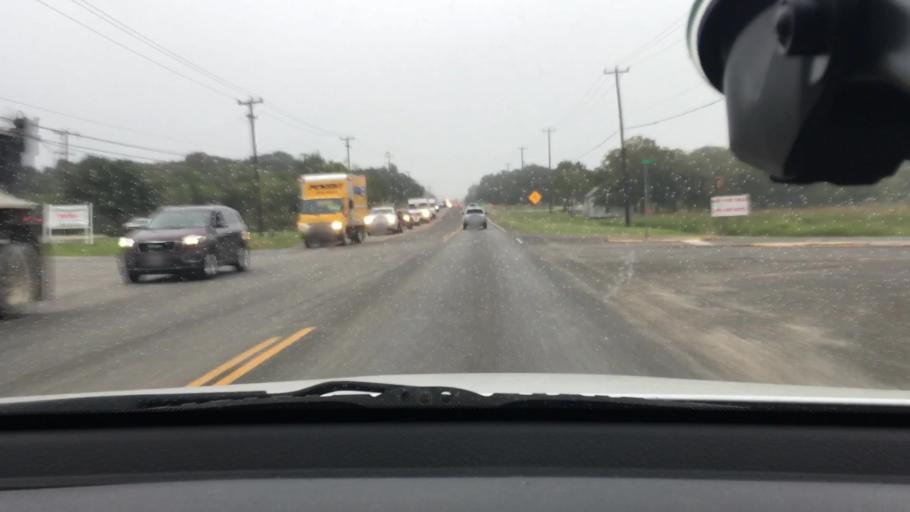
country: US
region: Texas
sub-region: Comal County
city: Garden Ridge
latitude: 29.6133
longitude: -98.3191
